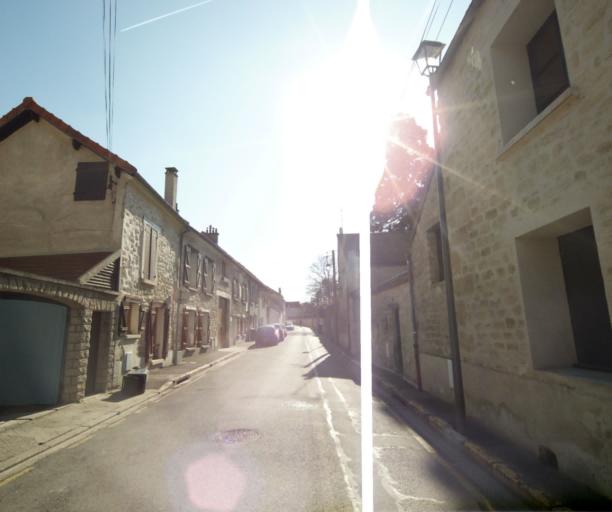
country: FR
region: Ile-de-France
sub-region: Departement du Val-d'Oise
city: Neuville-sur-Oise
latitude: 49.0267
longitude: 2.0582
